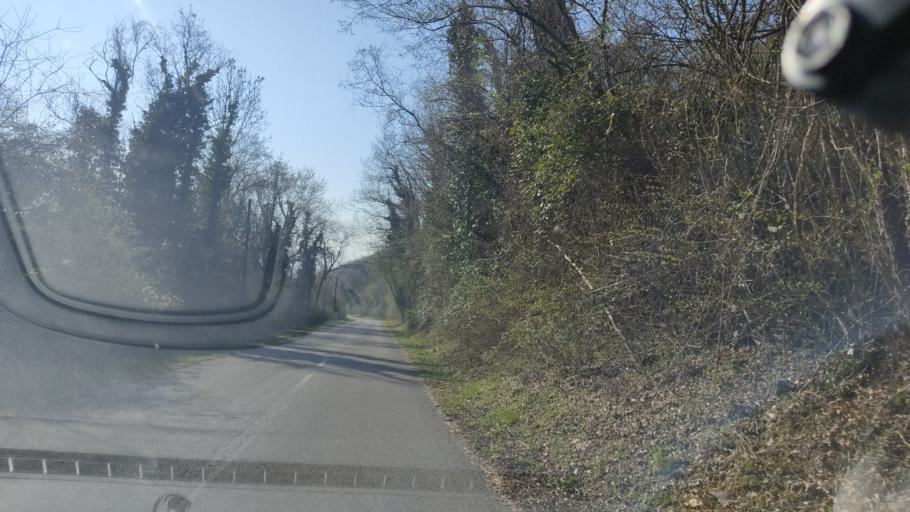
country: IT
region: Friuli Venezia Giulia
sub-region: Provincia di Pordenone
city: Polcenigo
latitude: 46.0663
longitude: 12.5130
